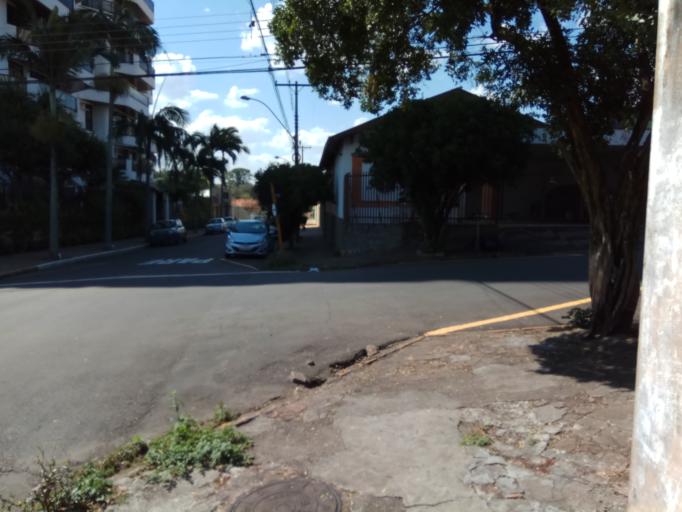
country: BR
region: Sao Paulo
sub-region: Piracicaba
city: Piracicaba
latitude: -22.7118
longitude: -47.6439
